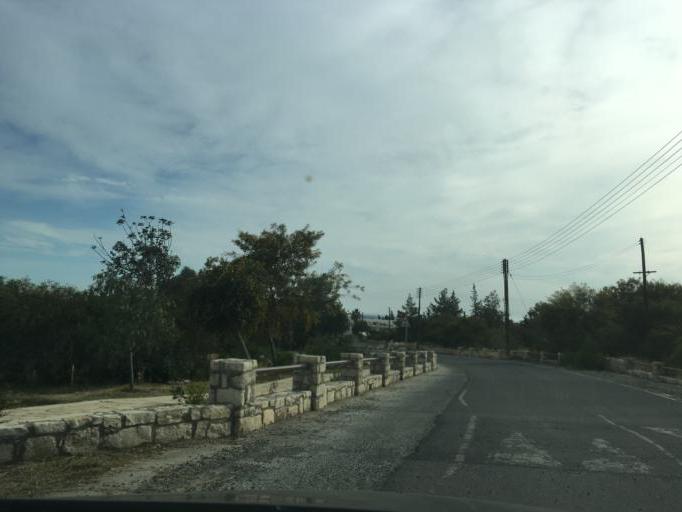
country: CY
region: Limassol
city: Pano Polemidia
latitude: 34.7123
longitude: 33.0055
